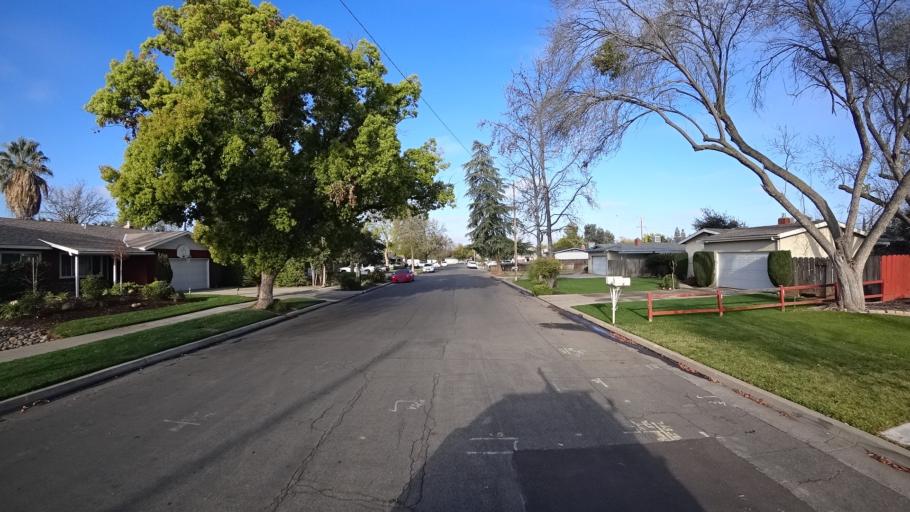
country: US
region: California
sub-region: Fresno County
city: Fresno
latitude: 36.8202
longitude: -119.7929
